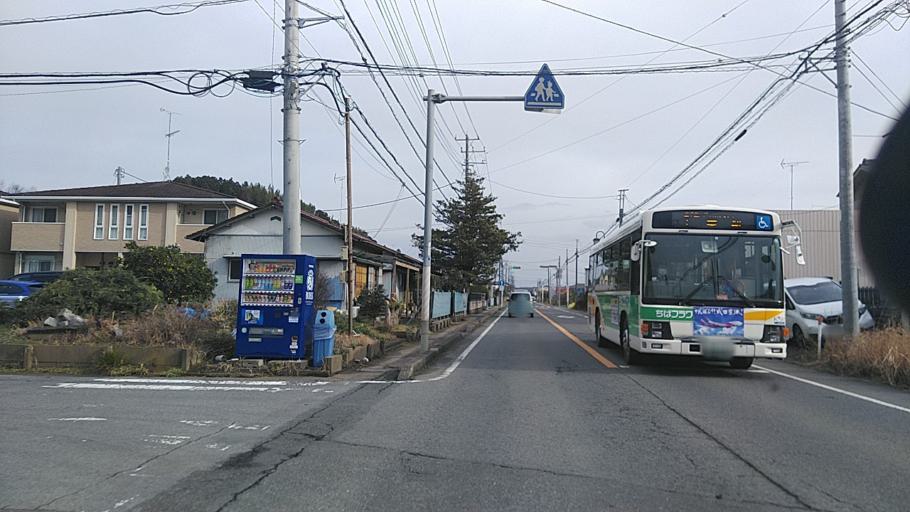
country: JP
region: Chiba
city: Togane
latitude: 35.5767
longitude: 140.3750
